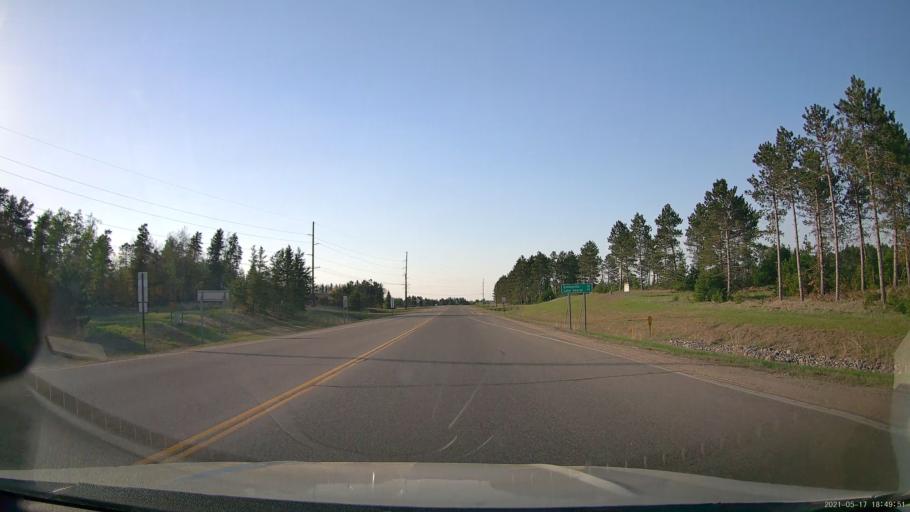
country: US
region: Minnesota
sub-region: Hubbard County
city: Park Rapids
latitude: 46.9263
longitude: -95.0157
